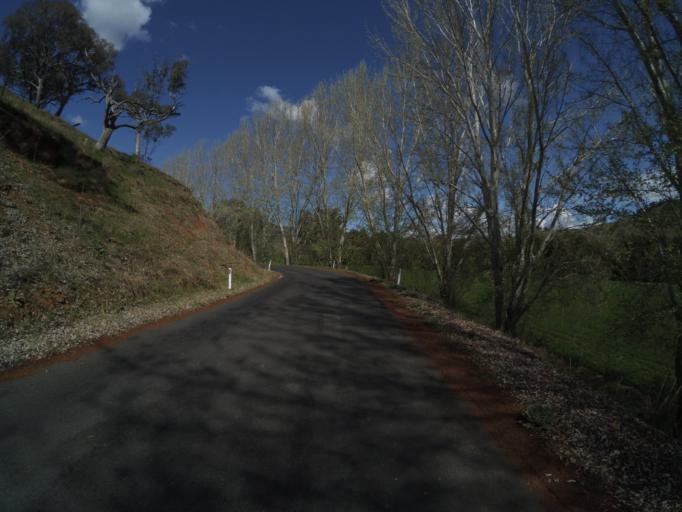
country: AU
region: New South Wales
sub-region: Yass Valley
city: Murrumbateman
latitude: -35.0354
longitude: 148.8363
